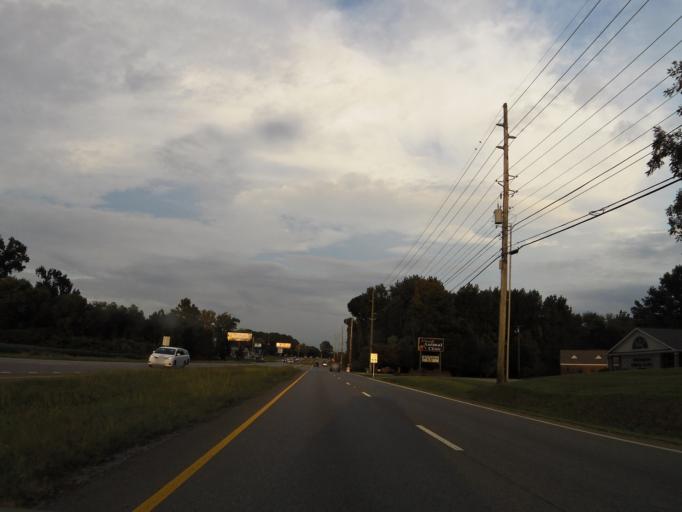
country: US
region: Alabama
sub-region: Madison County
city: Madison
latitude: 34.7568
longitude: -86.7231
